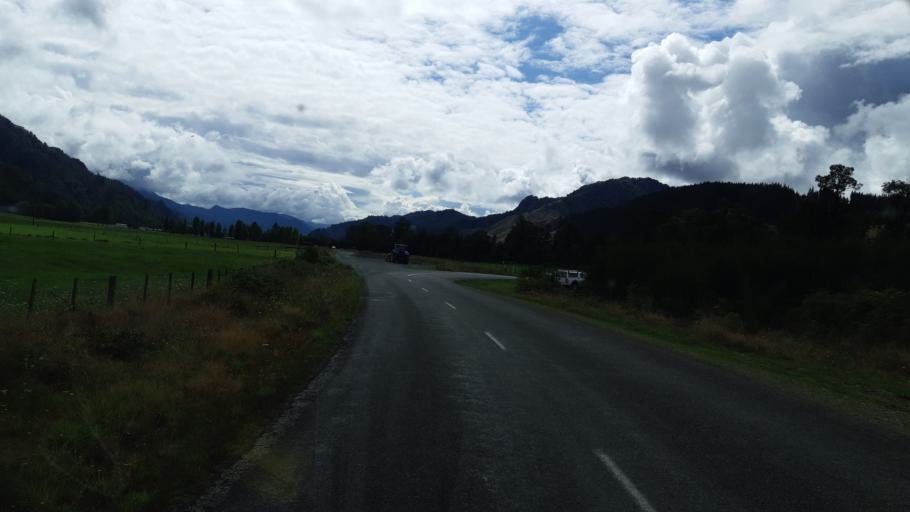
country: NZ
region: Tasman
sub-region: Tasman District
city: Wakefield
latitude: -41.7732
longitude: 172.3771
